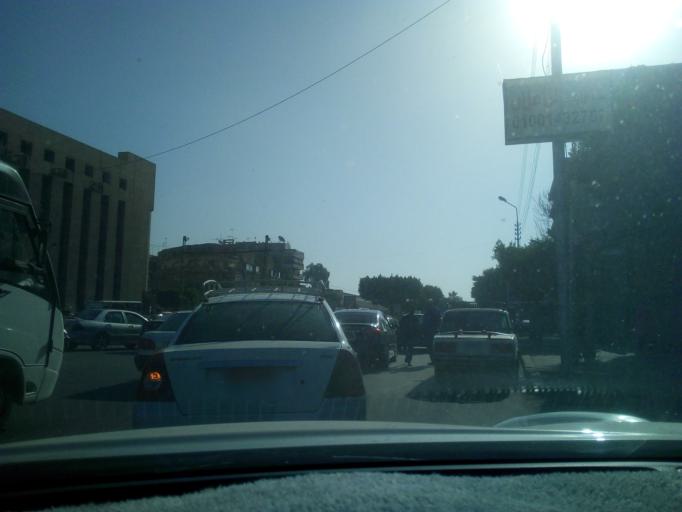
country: EG
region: Muhafazat al Qahirah
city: Cairo
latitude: 30.1033
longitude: 31.3287
